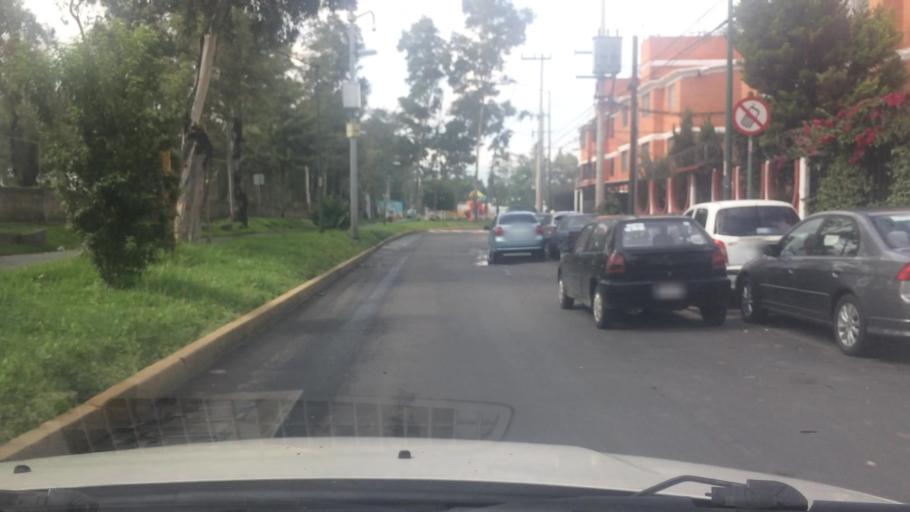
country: MX
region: Mexico City
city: Xochimilco
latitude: 19.3084
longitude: -99.1002
